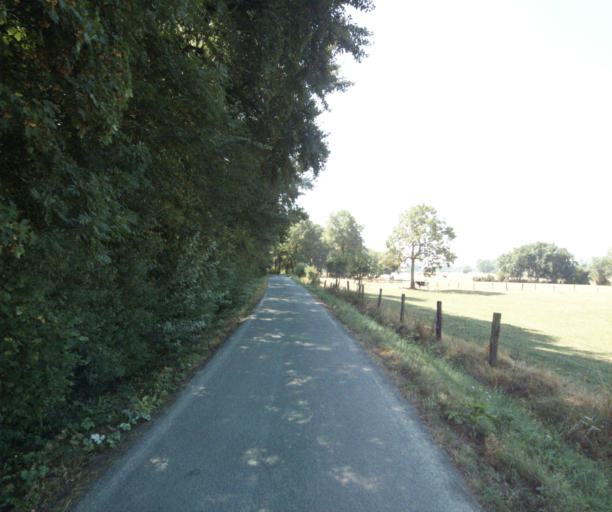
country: FR
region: Nord-Pas-de-Calais
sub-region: Departement du Nord
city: Wervicq-Sud
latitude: 50.7640
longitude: 3.0415
